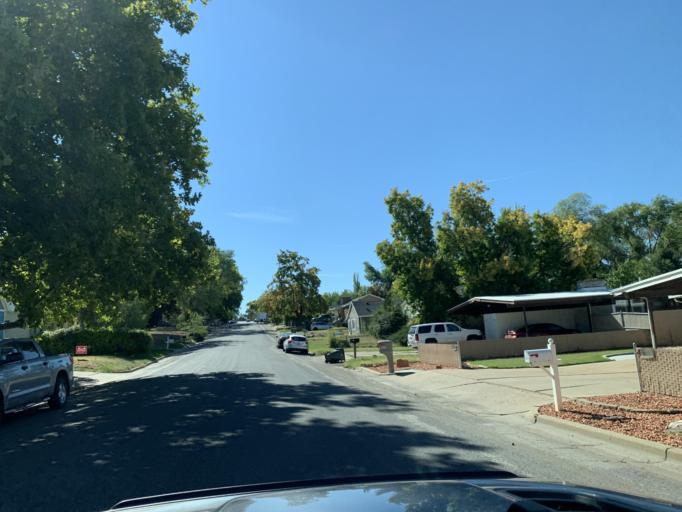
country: US
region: Utah
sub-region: Weber County
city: South Ogden
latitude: 41.1936
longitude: -111.9642
